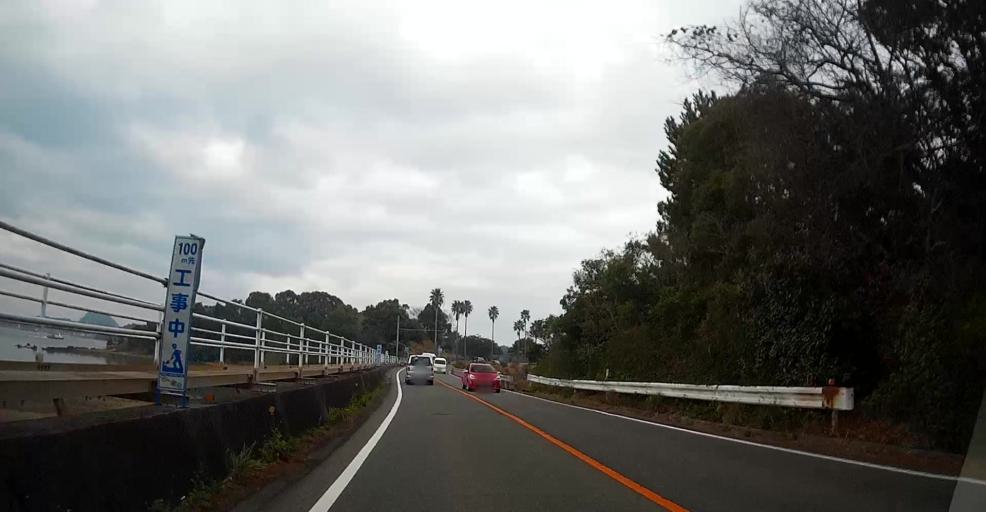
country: JP
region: Kumamoto
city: Yatsushiro
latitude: 32.5339
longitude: 130.4231
